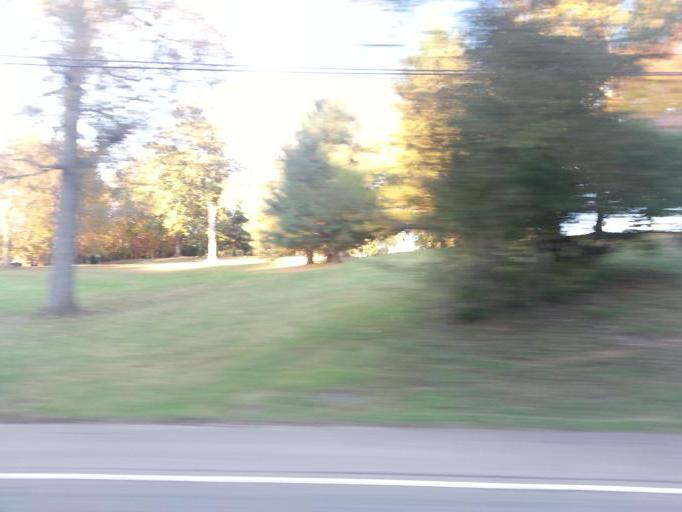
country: US
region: Tennessee
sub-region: Knox County
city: Knoxville
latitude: 35.9244
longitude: -83.9972
